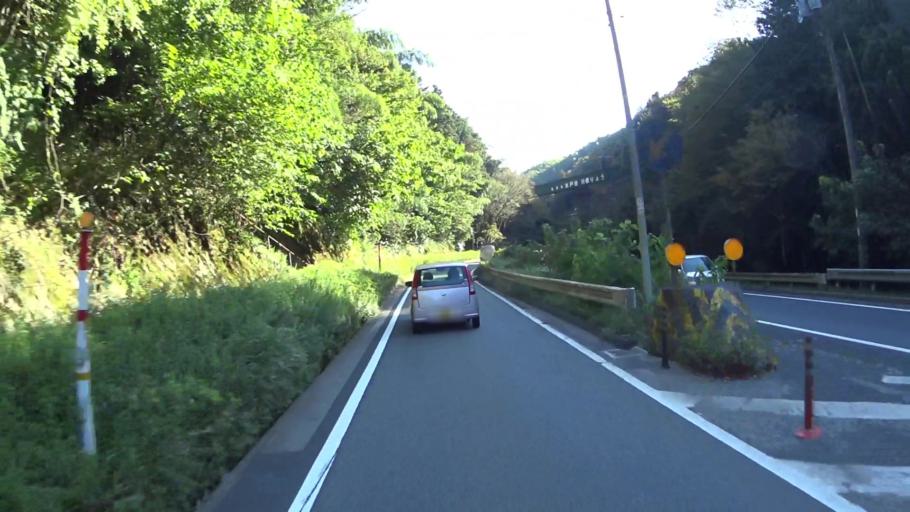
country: JP
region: Kyoto
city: Miyazu
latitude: 35.5428
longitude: 135.1108
